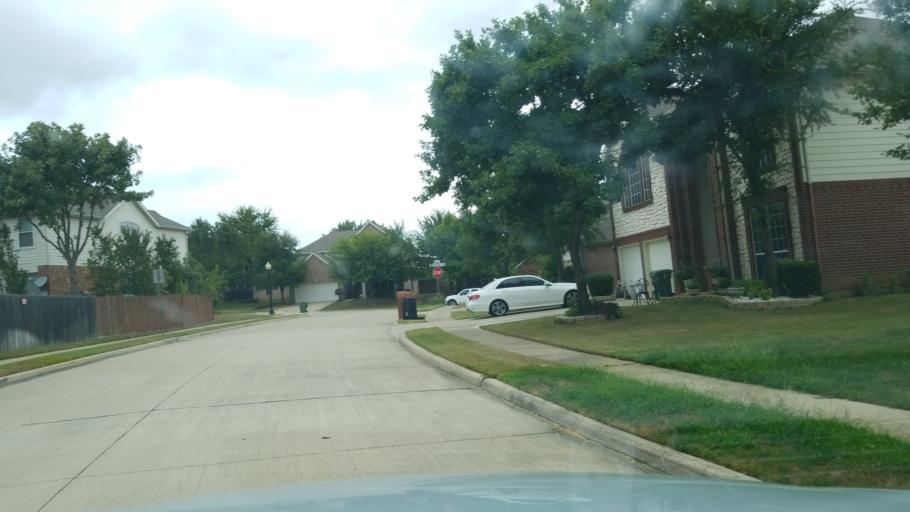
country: US
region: Texas
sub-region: Tarrant County
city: Euless
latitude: 32.8429
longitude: -97.1031
